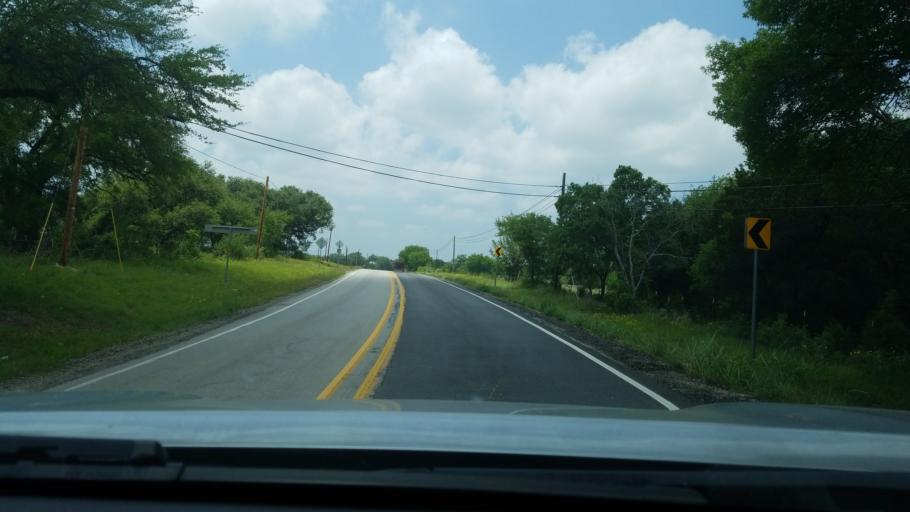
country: US
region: Texas
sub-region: Hays County
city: Dripping Springs
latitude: 30.1492
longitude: -98.0528
